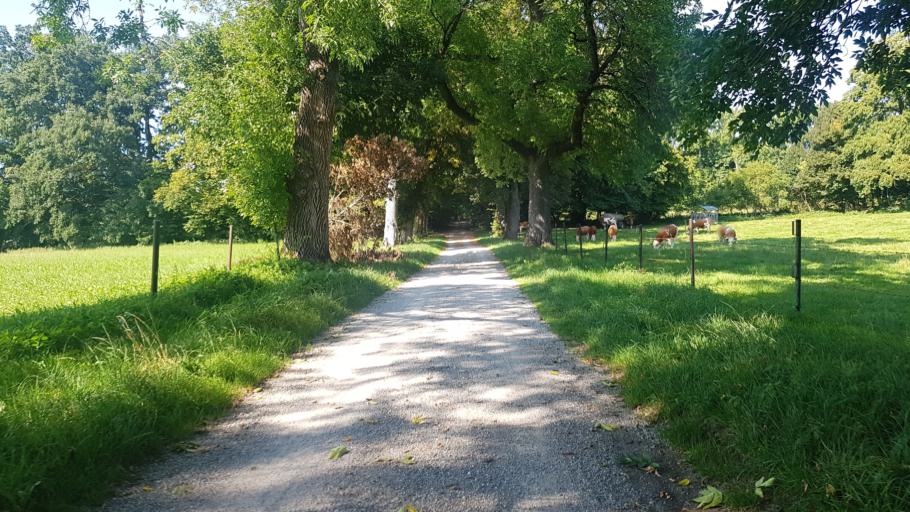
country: DE
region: Bavaria
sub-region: Upper Bavaria
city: Inning am Ammersee
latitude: 48.0452
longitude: 11.1362
